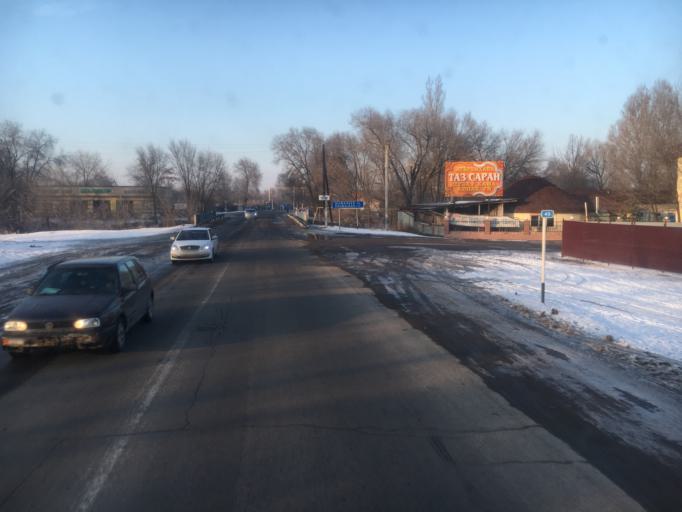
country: KZ
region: Almaty Oblysy
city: Burunday
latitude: 43.3657
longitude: 76.6416
